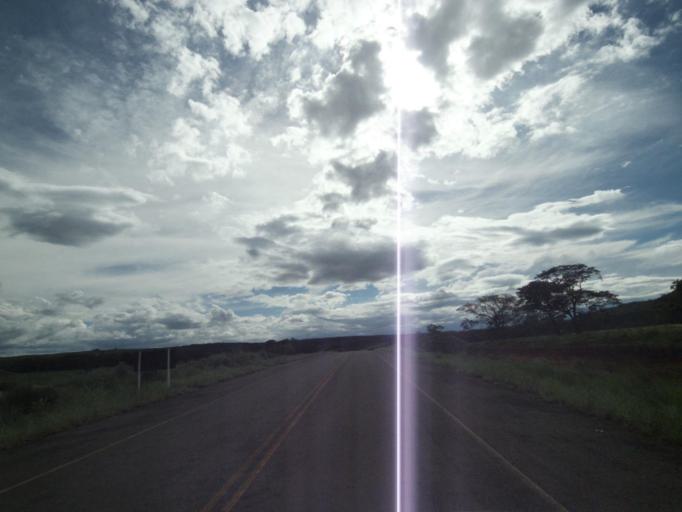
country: BR
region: Goias
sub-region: Jaragua
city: Jaragua
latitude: -15.8384
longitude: -49.2825
